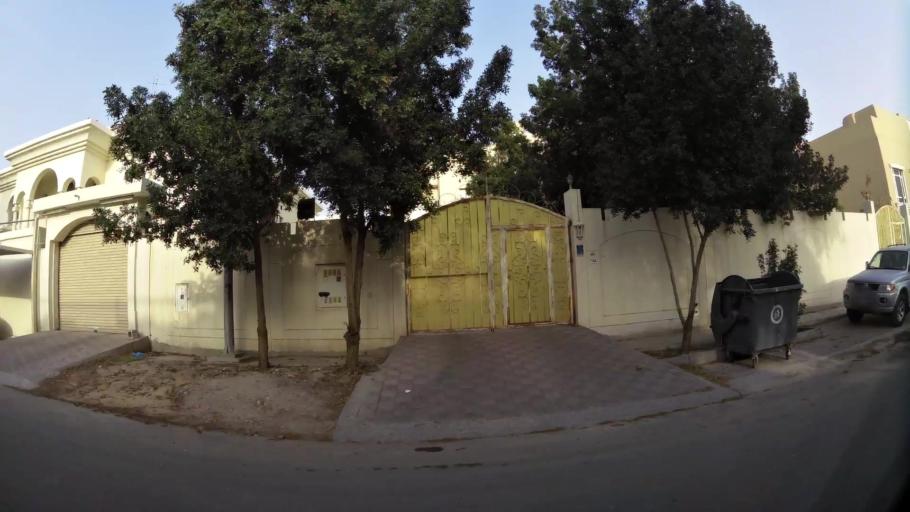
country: QA
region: Baladiyat ar Rayyan
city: Ar Rayyan
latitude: 25.2468
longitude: 51.4484
